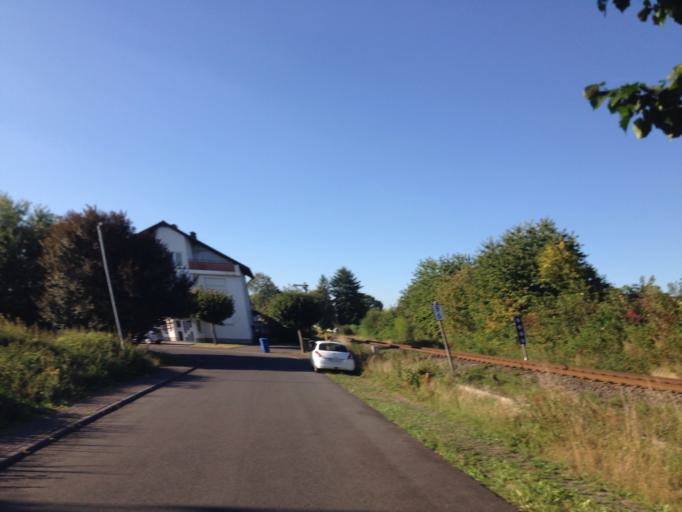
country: DE
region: Hesse
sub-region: Regierungsbezirk Giessen
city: Lich
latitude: 50.5334
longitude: 8.7490
